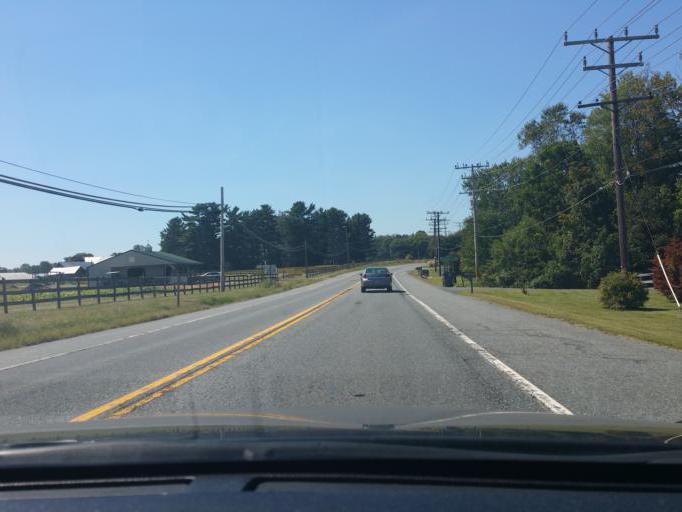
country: US
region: Maryland
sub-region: Harford County
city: Bel Air South
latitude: 39.5568
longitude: -76.2621
